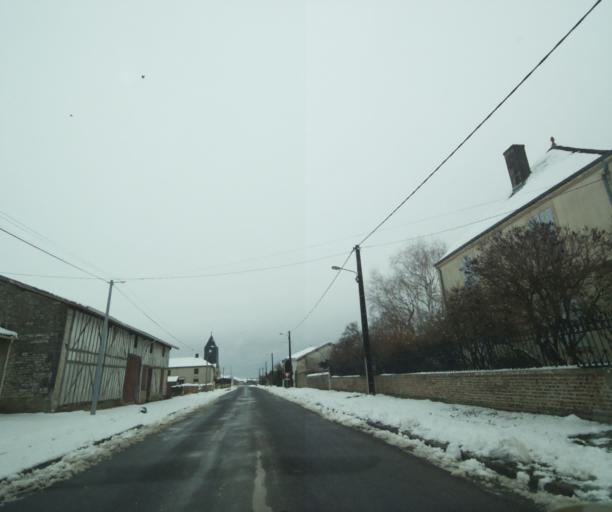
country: FR
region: Champagne-Ardenne
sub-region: Departement de la Haute-Marne
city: Montier-en-Der
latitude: 48.4371
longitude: 4.8016
